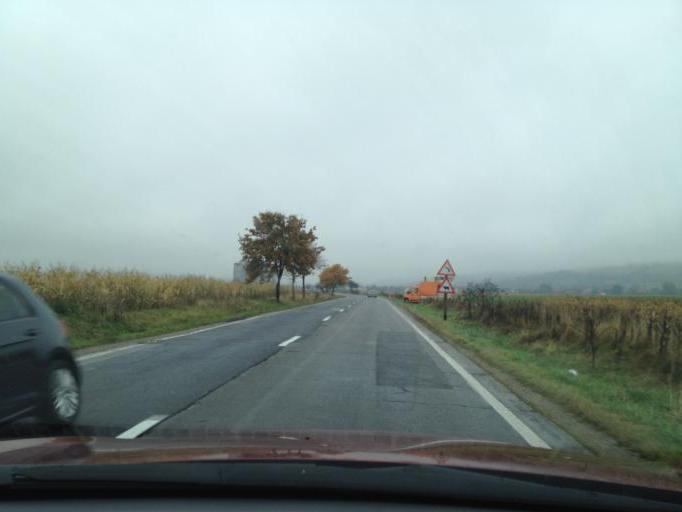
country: RO
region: Brasov
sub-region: Comuna Zarnesti
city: Tohanu Nou
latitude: 45.5583
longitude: 25.3959
